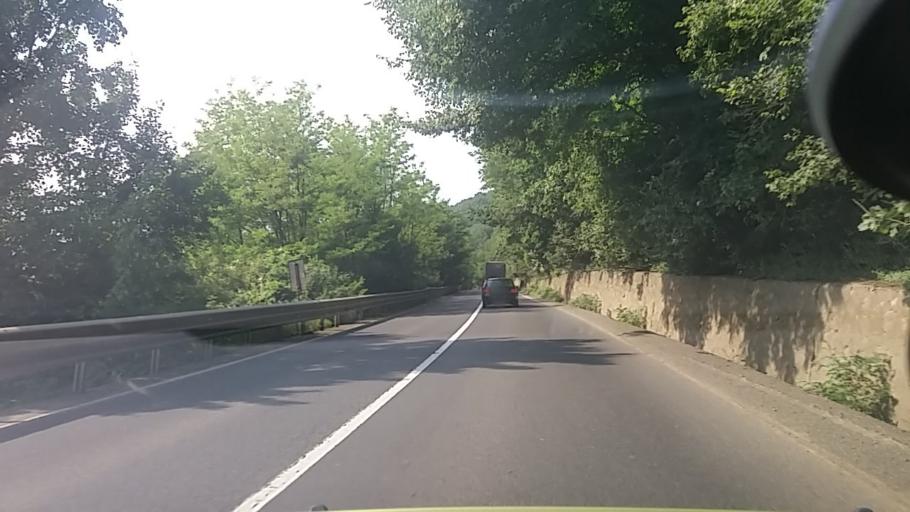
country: RO
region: Arad
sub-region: Comuna Bata
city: Bata
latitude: 46.0643
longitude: 22.0436
